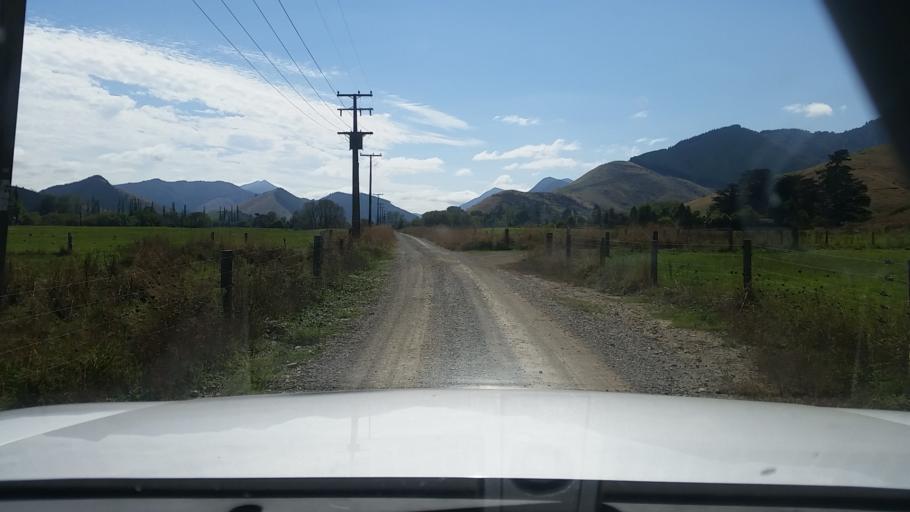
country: NZ
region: Nelson
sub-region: Nelson City
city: Nelson
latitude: -41.2593
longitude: 173.5815
